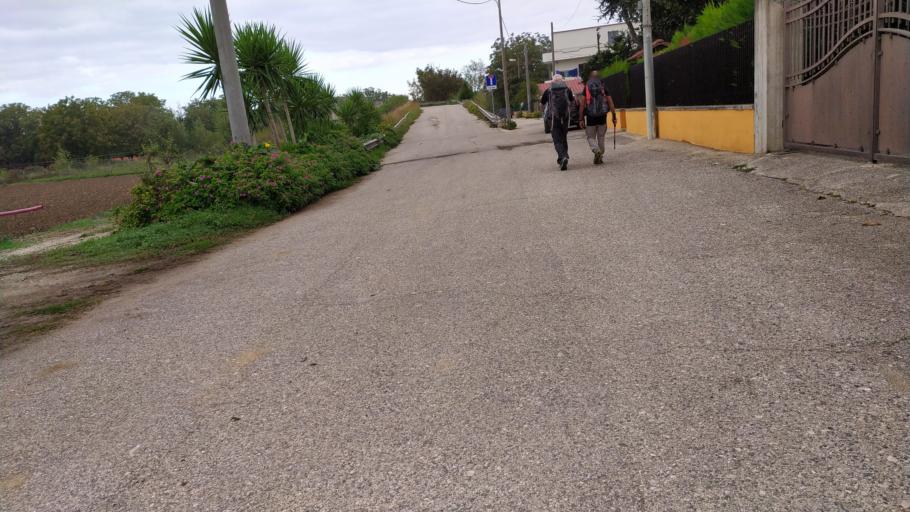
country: IT
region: Campania
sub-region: Provincia di Caserta
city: Montedecoro
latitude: 41.0095
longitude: 14.4111
